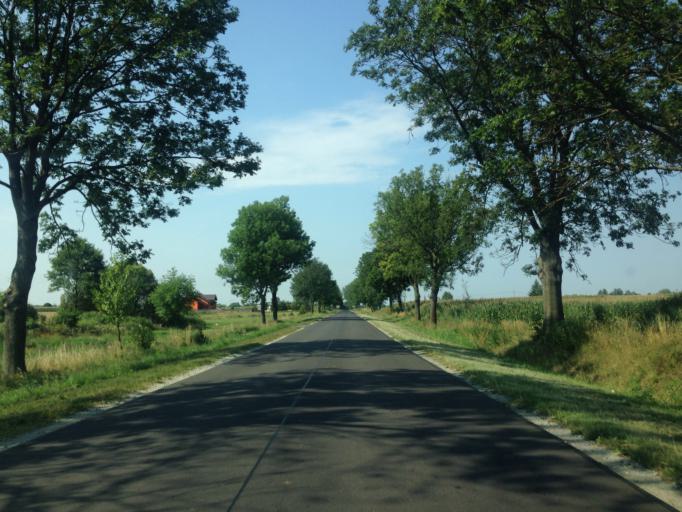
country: PL
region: Kujawsko-Pomorskie
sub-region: Powiat brodnicki
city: Swiedziebnia
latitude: 53.1170
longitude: 19.5018
